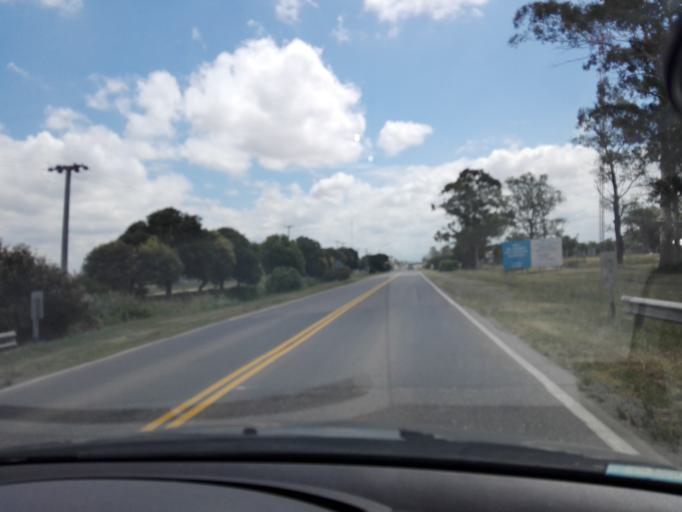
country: AR
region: Cordoba
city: Toledo
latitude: -31.6480
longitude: -64.0830
